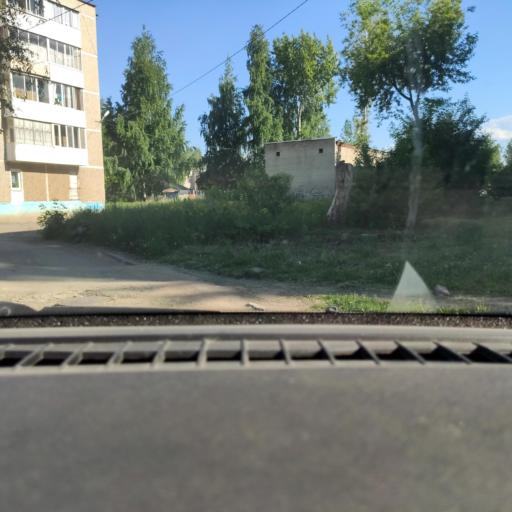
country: RU
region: Perm
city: Krasnokamsk
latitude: 58.0873
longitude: 55.7799
